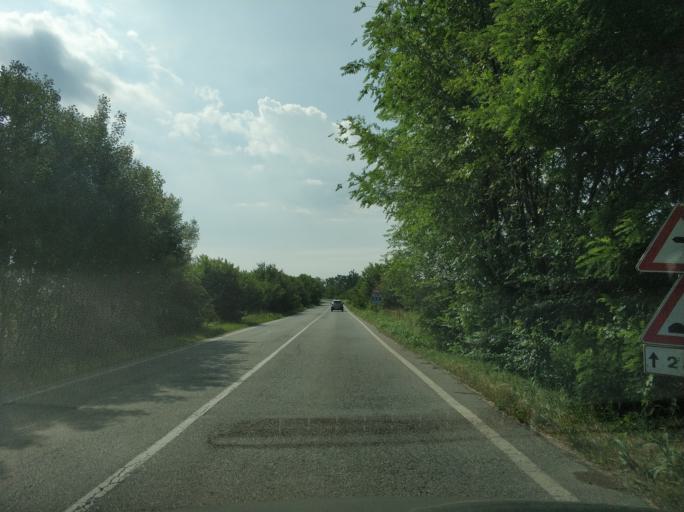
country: IT
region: Piedmont
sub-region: Provincia di Torino
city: Pralormo
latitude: 44.8769
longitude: 7.8849
